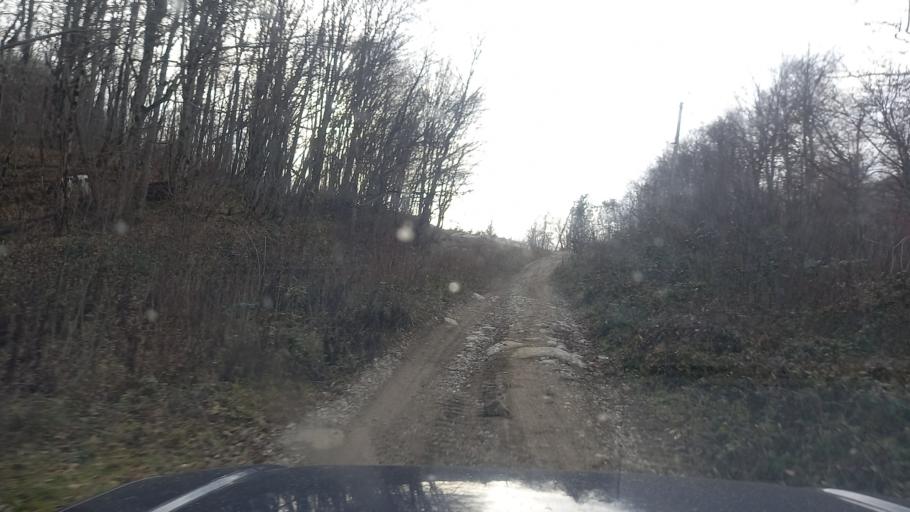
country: RU
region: Krasnodarskiy
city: Neftegorsk
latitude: 44.2142
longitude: 39.7132
